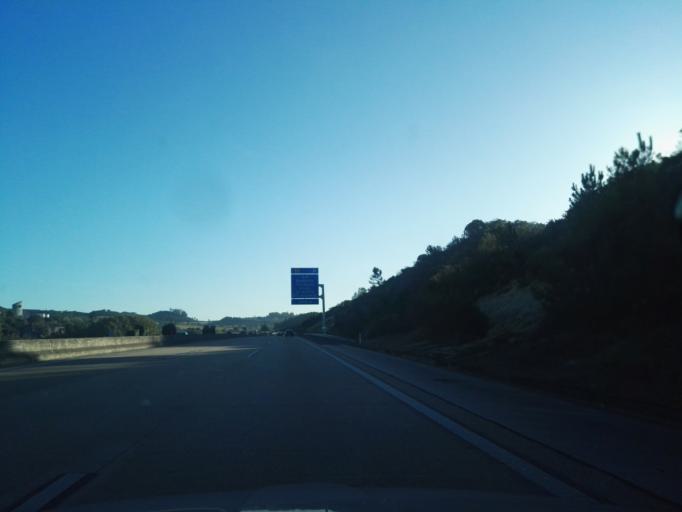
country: PT
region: Lisbon
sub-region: Loures
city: Bucelas
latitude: 38.9012
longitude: -9.0988
